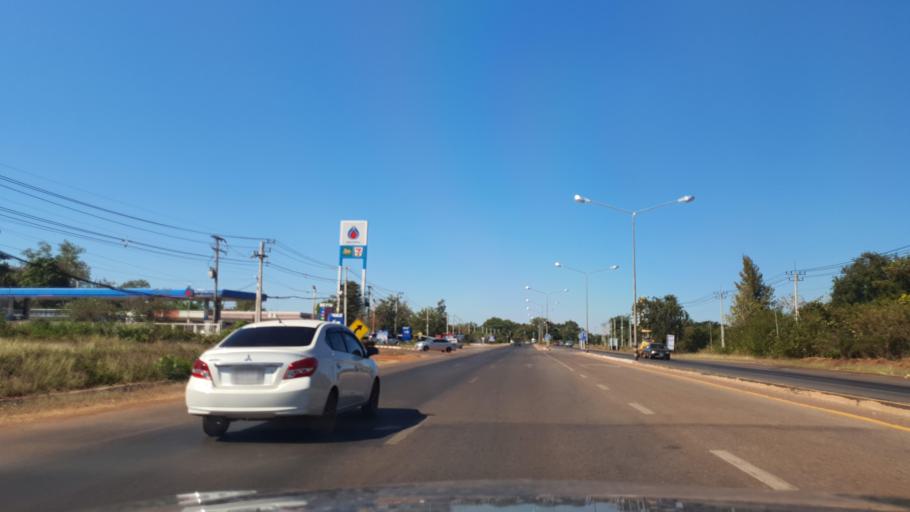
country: TH
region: Sakon Nakhon
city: Sakon Nakhon
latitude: 17.2568
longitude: 104.1678
